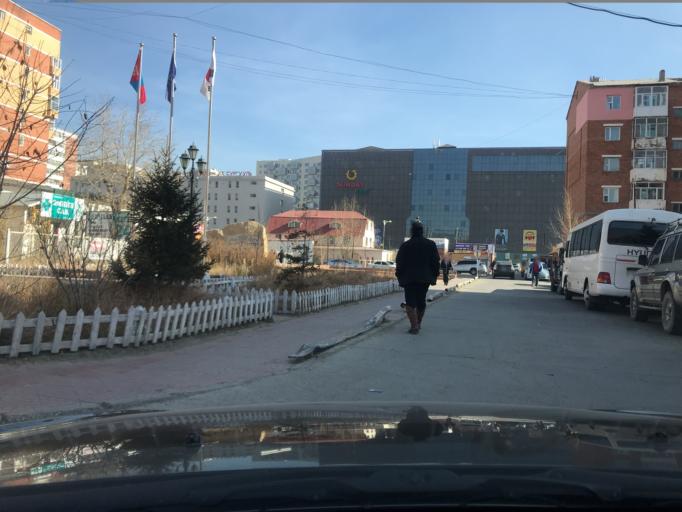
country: MN
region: Ulaanbaatar
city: Ulaanbaatar
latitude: 47.9110
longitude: 106.9420
